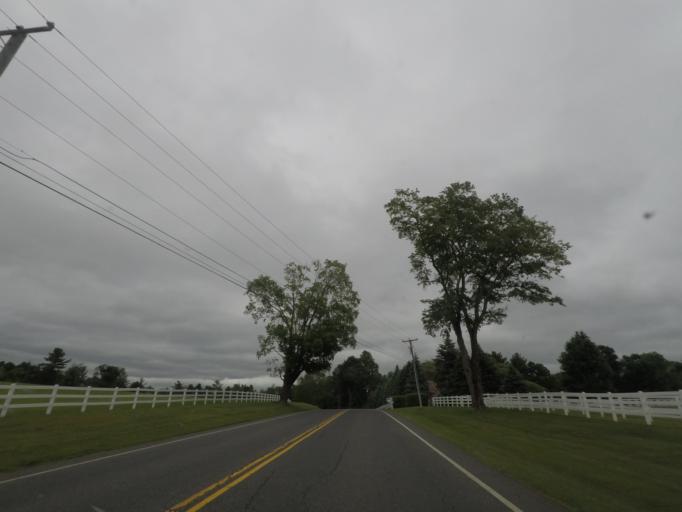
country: US
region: Connecticut
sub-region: Litchfield County
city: Canaan
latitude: 41.9292
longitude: -73.4117
